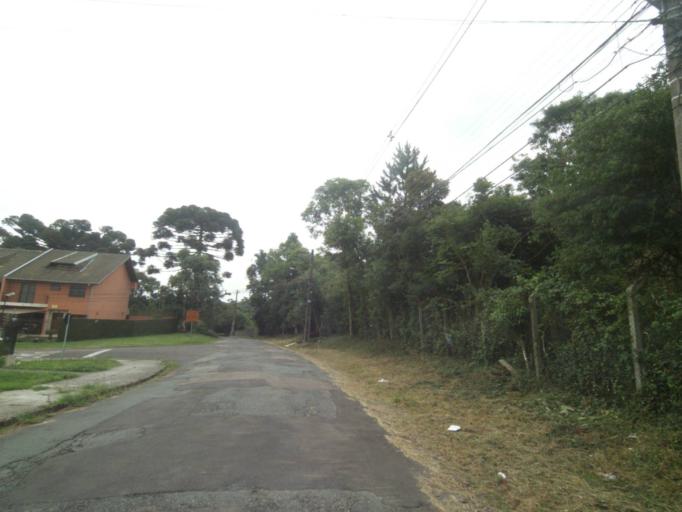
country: BR
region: Parana
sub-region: Curitiba
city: Curitiba
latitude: -25.4040
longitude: -49.2952
